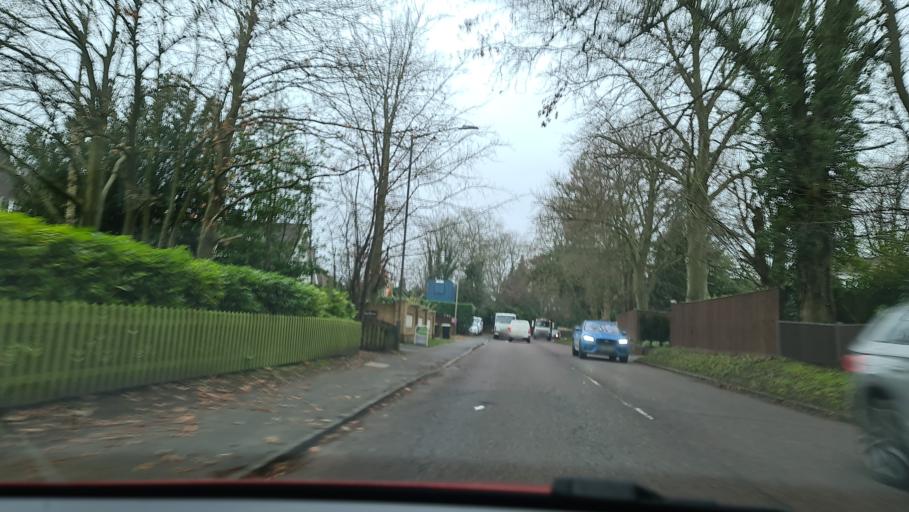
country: GB
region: England
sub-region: Buckinghamshire
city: Beaconsfield
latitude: 51.6176
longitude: -0.6490
